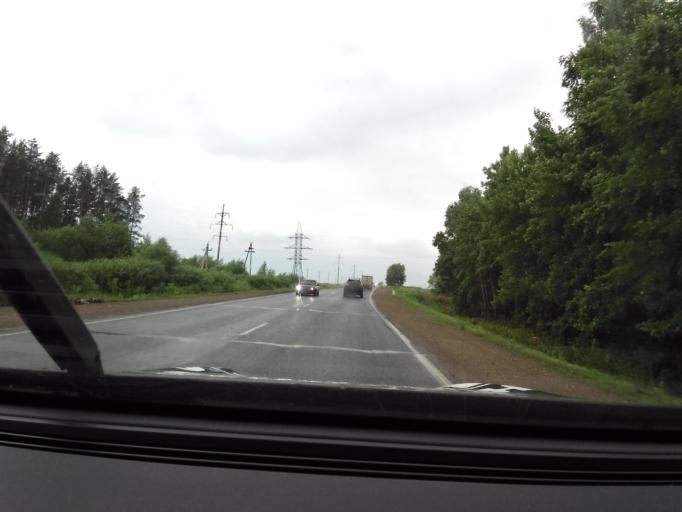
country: RU
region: Bashkortostan
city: Mikhaylovka
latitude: 54.8457
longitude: 55.7824
